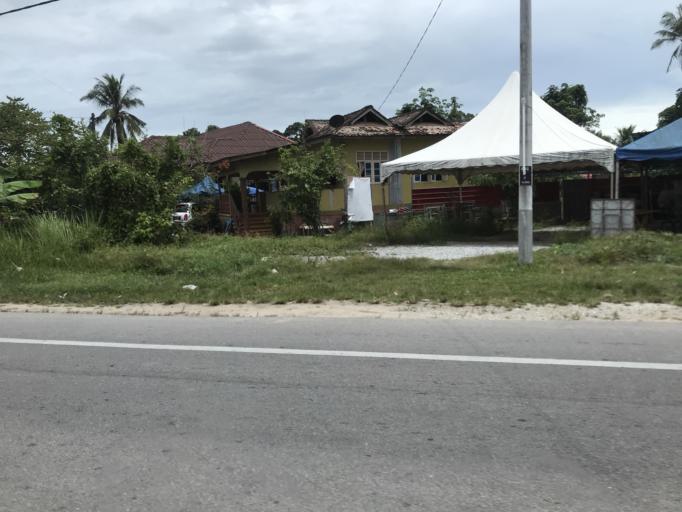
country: MY
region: Kelantan
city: Tumpat
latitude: 6.1694
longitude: 102.1907
